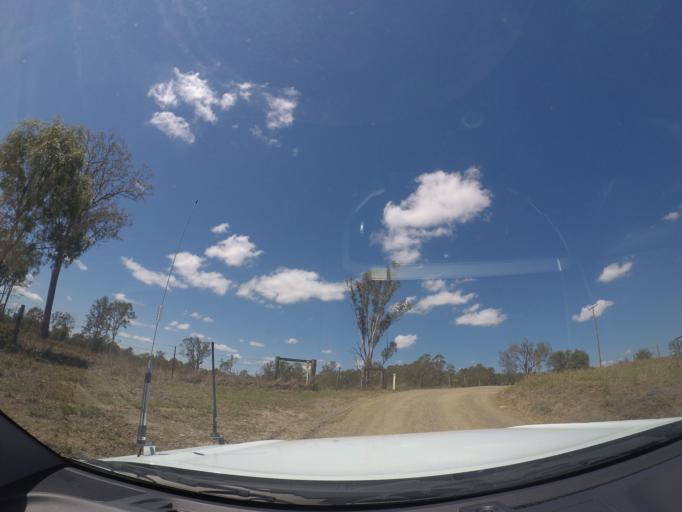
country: AU
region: Queensland
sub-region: Logan
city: Cedar Vale
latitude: -27.8509
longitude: 152.8878
